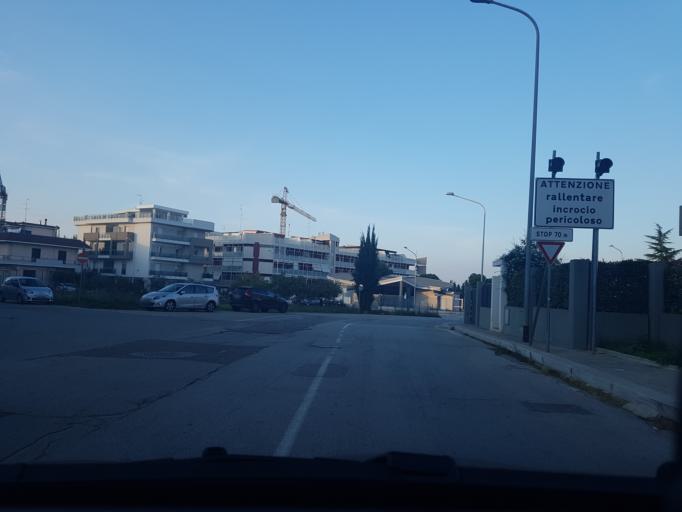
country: IT
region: Apulia
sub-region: Provincia di Bari
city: Bitritto
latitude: 41.0452
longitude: 16.8305
